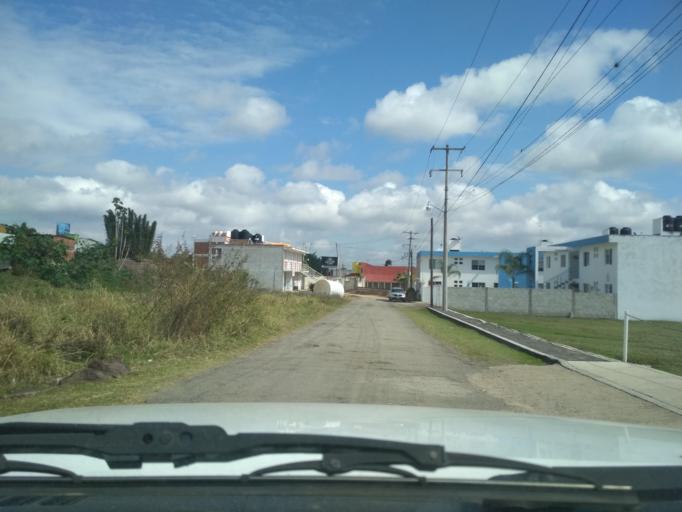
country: MX
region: Veracruz
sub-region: Emiliano Zapata
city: Dos Rios
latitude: 19.4832
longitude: -96.8109
